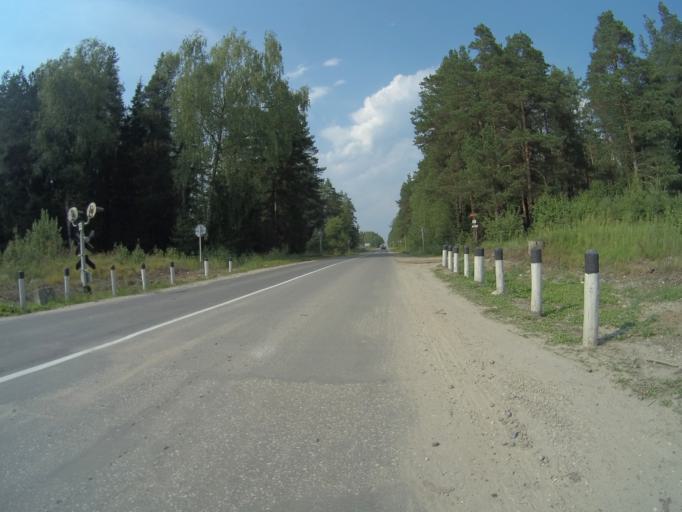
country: RU
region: Vladimir
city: Andreyevo
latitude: 55.9446
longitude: 41.1329
